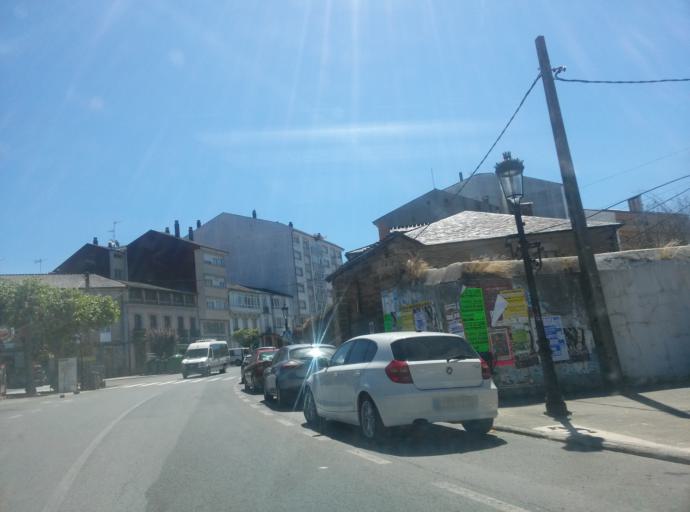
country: ES
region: Galicia
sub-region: Provincia de Lugo
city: Meira
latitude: 43.2139
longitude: -7.2939
